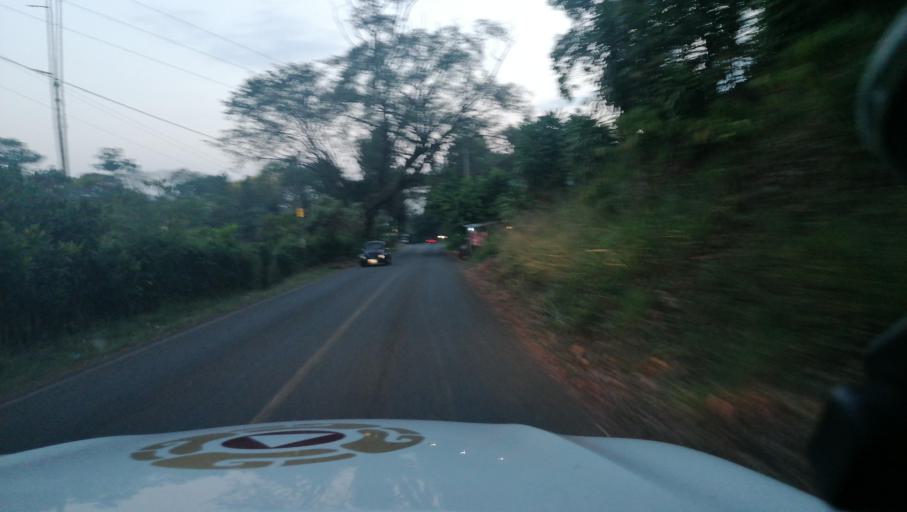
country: MX
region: Chiapas
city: Veinte de Noviembre
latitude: 15.0197
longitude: -92.2444
